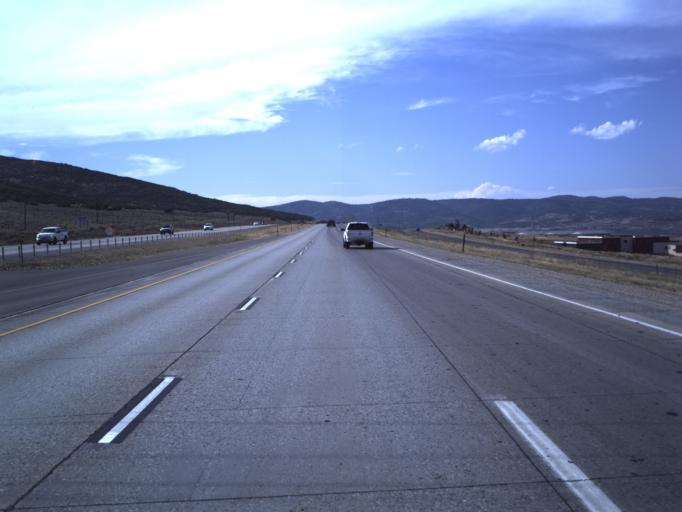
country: US
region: Utah
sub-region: Summit County
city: Park City
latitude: 40.6890
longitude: -111.4658
